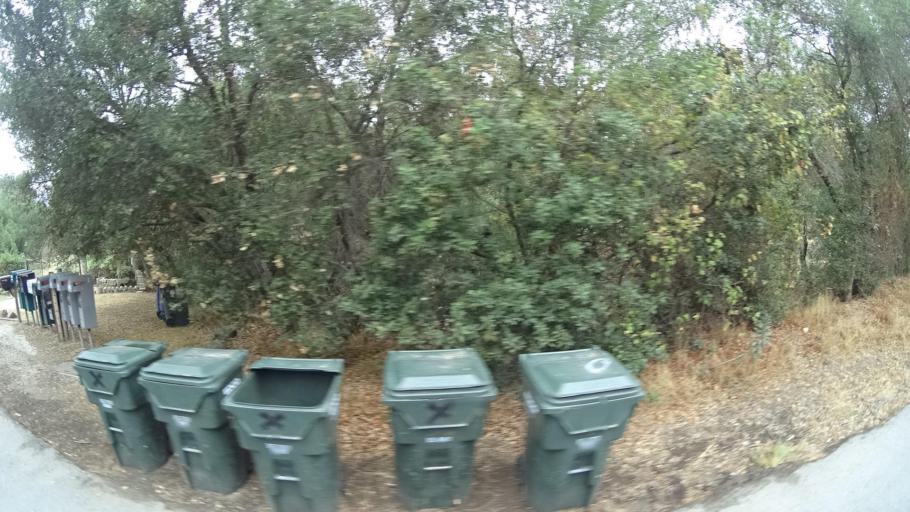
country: US
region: California
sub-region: San Diego County
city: Lake San Marcos
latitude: 33.0778
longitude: -117.1648
